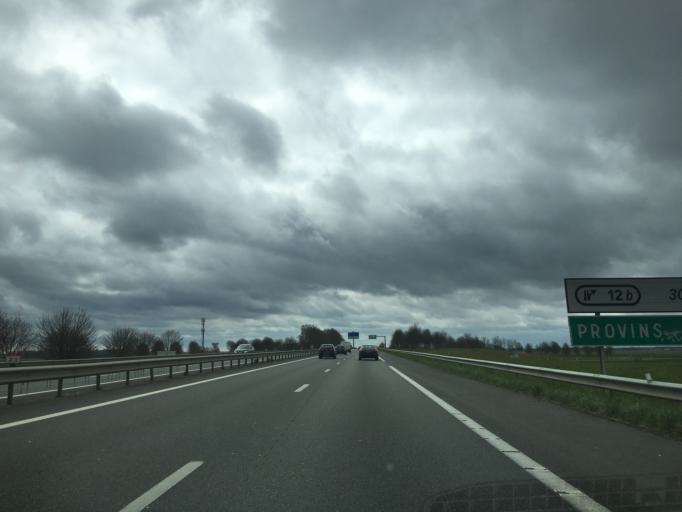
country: FR
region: Ile-de-France
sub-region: Departement de Seine-et-Marne
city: Moissy-Cramayel
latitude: 48.6353
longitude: 2.6287
